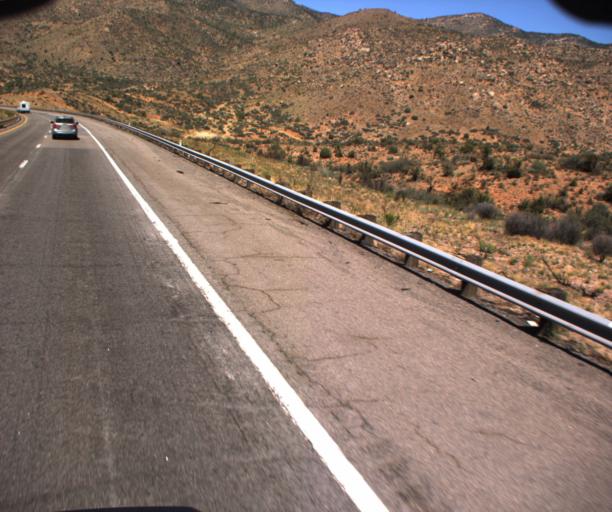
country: US
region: Arizona
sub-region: Mohave County
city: Peach Springs
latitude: 35.1714
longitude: -113.5155
